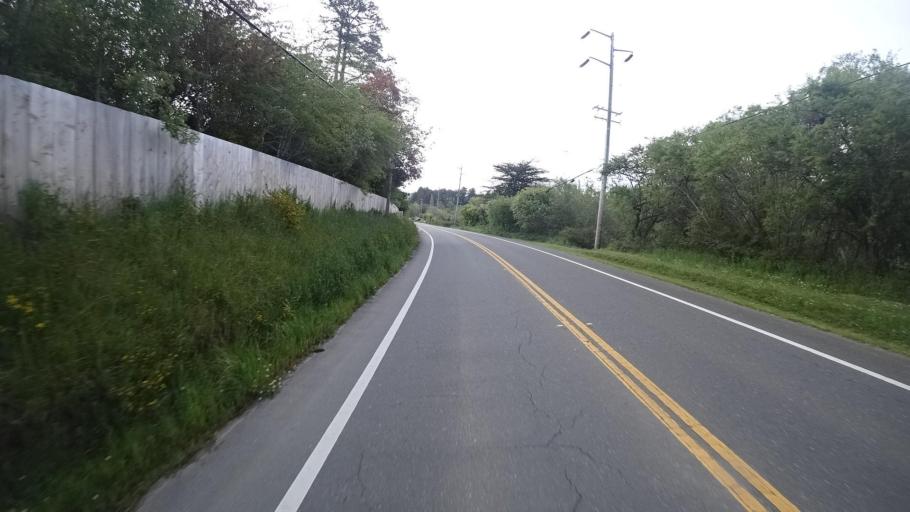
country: US
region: California
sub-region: Humboldt County
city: Myrtletown
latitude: 40.7666
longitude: -124.0679
